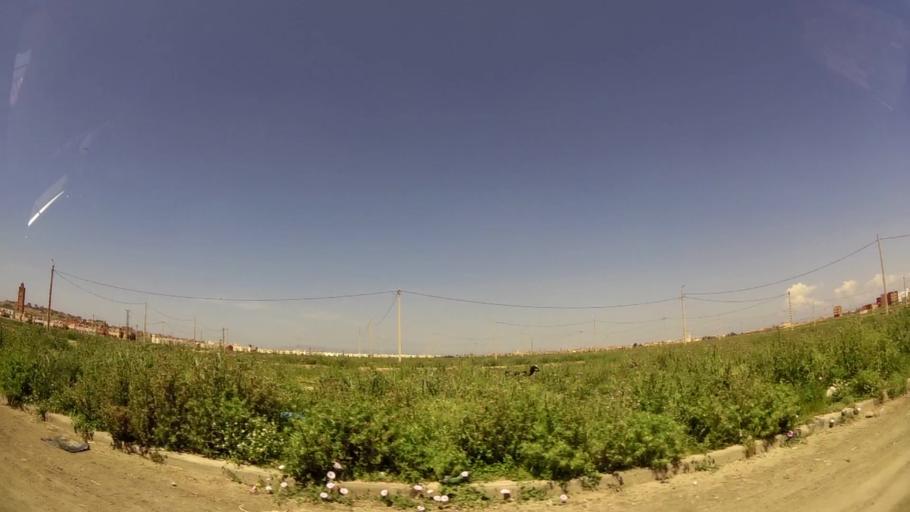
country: MA
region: Oriental
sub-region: Oujda-Angad
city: Oujda
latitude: 34.6918
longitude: -1.9358
